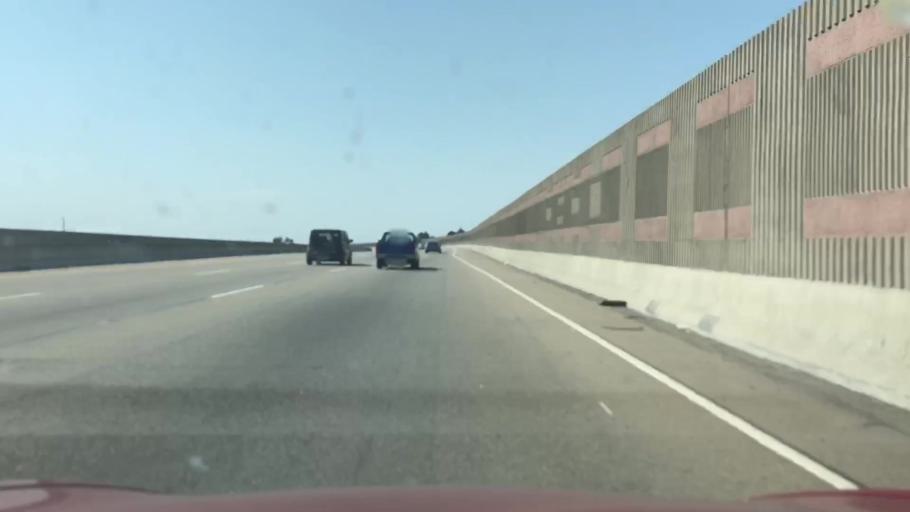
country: US
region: California
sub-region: Alameda County
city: Oakland
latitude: 37.8022
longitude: -122.2819
